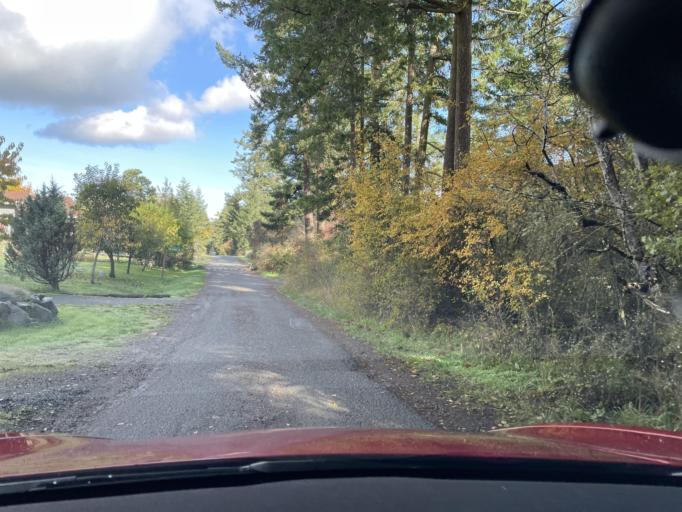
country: US
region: Washington
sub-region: San Juan County
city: Friday Harbor
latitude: 48.4988
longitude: -123.0230
